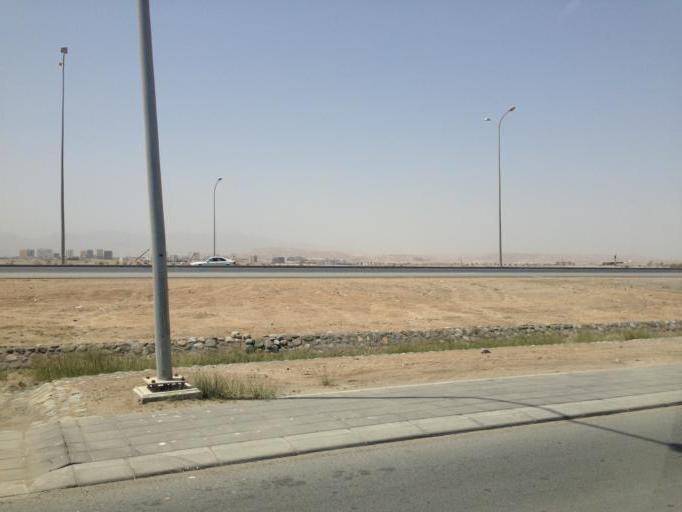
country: OM
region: Muhafazat Masqat
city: Bawshar
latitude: 23.6030
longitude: 58.3458
